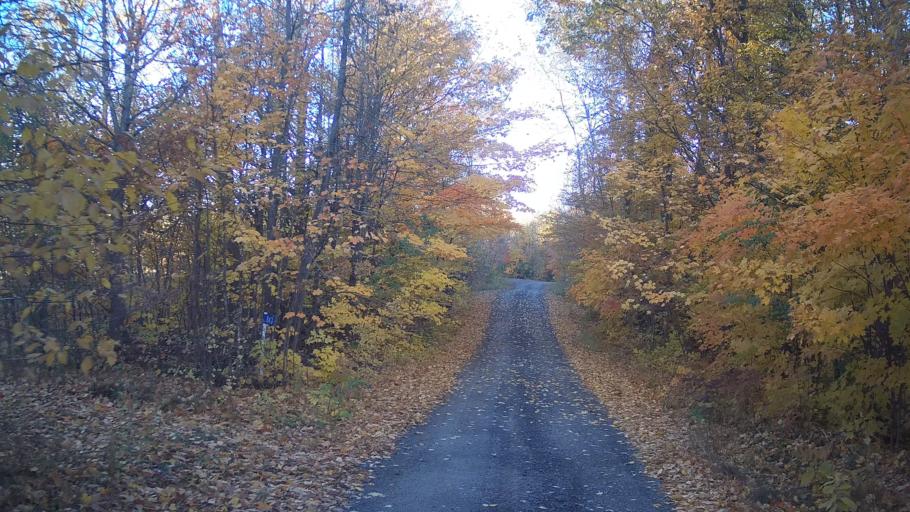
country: CA
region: Ontario
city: Arnprior
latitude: 45.3320
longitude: -76.3691
